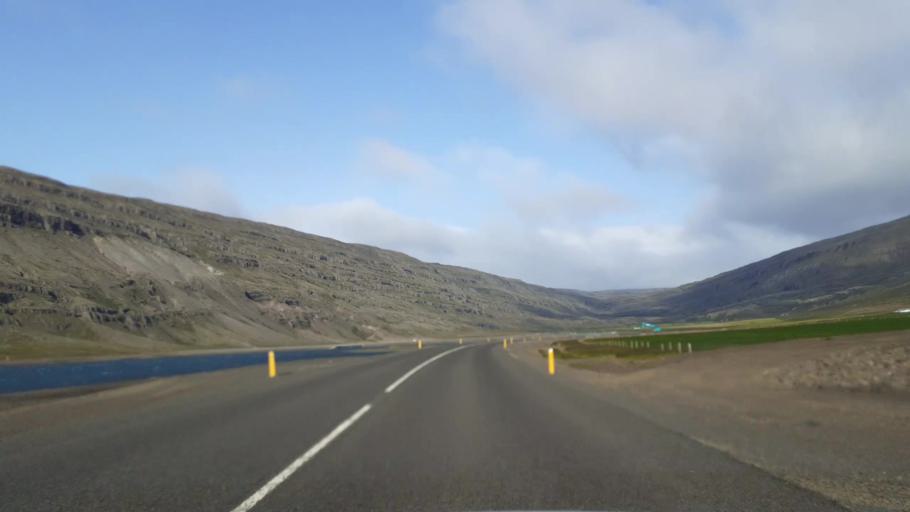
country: IS
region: East
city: Reydarfjoerdur
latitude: 64.7885
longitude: -14.4673
